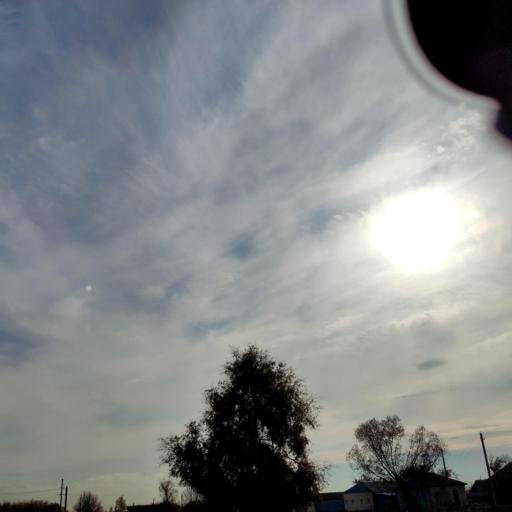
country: RU
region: Voronezj
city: Rossosh'
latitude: 51.1961
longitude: 38.7779
